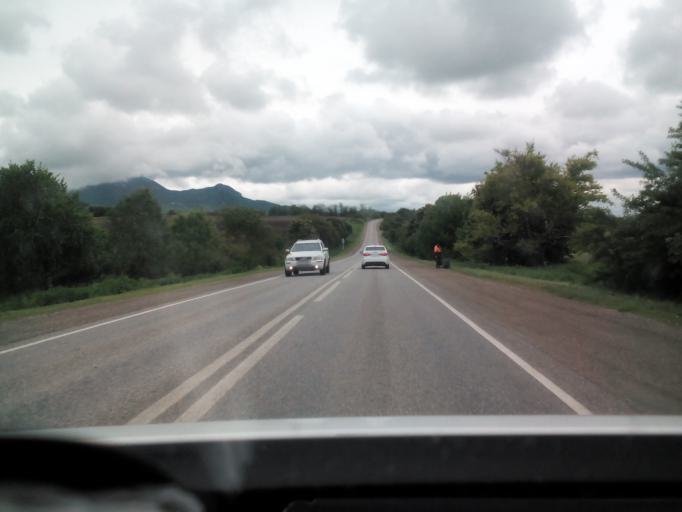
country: RU
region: Stavropol'skiy
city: Vinsady
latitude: 44.0703
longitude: 42.9231
